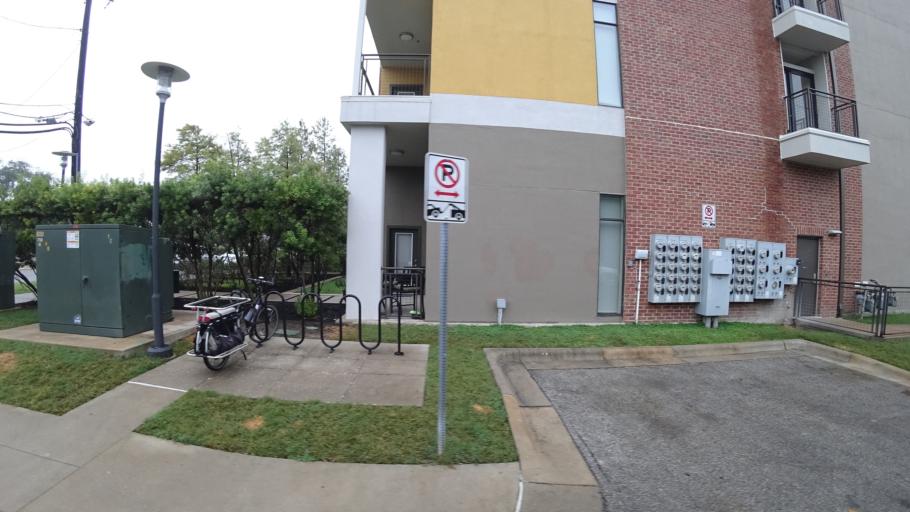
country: US
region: Texas
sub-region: Travis County
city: Austin
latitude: 30.2632
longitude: -97.7589
